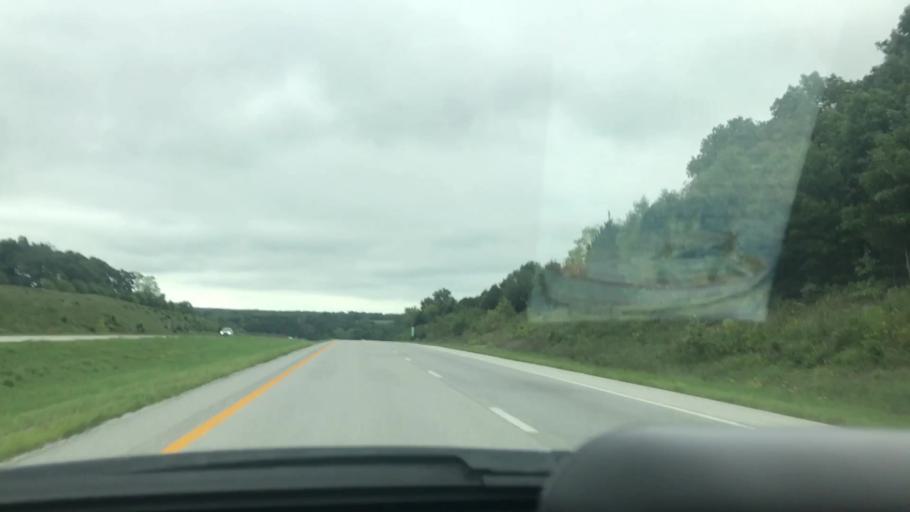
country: US
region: Missouri
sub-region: Greene County
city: Strafford
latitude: 37.2866
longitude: -93.1904
